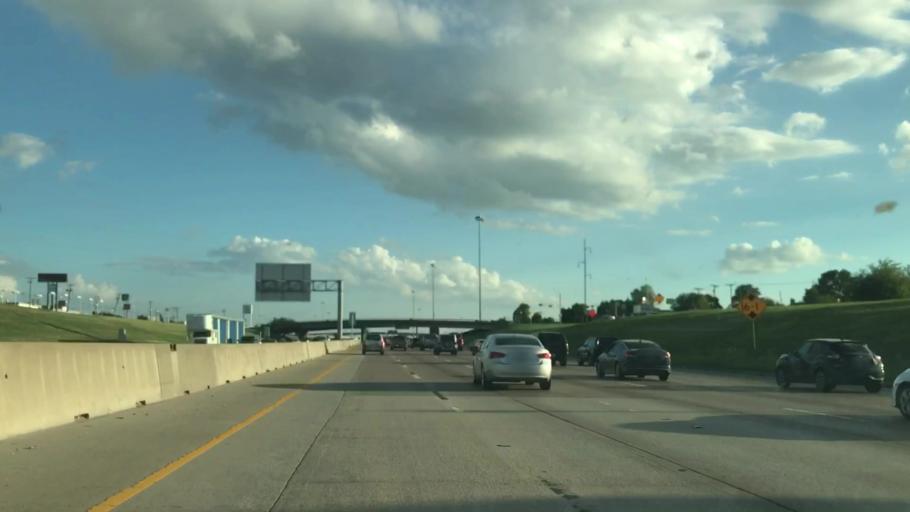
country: US
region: Texas
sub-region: Dallas County
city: Mesquite
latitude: 32.8348
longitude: -96.6324
